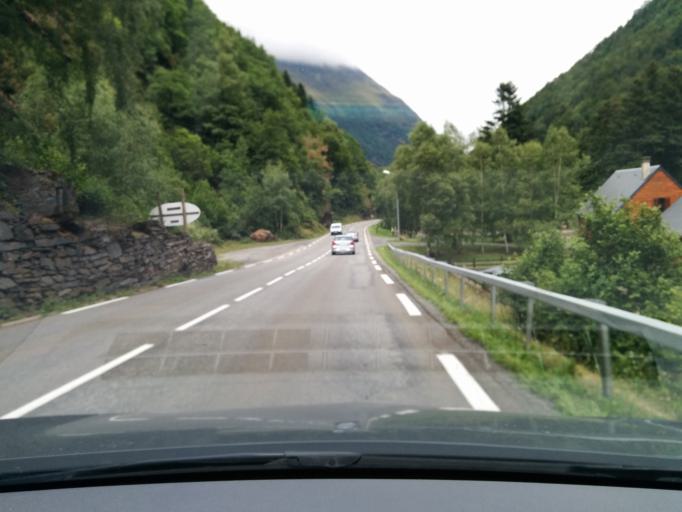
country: FR
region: Midi-Pyrenees
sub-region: Departement des Hautes-Pyrenees
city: Saint-Lary-Soulan
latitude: 42.7879
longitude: 0.2562
